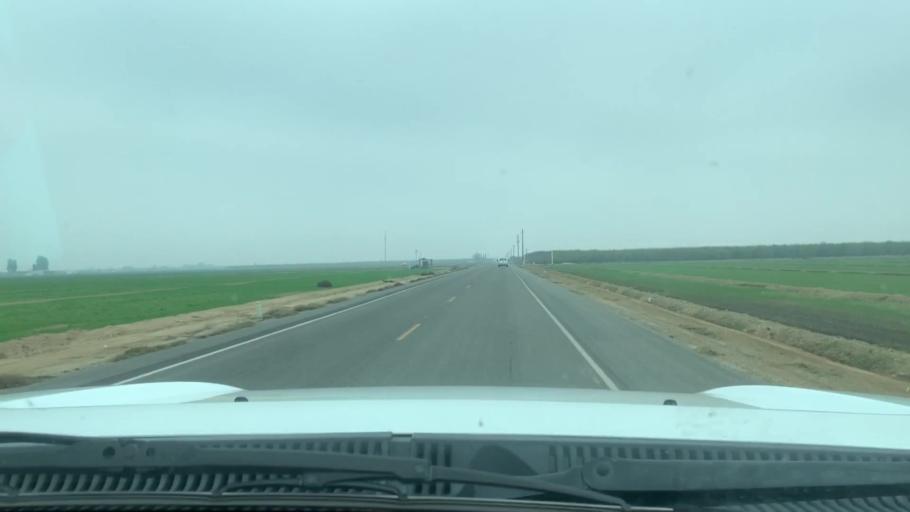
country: US
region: California
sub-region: Kern County
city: Wasco
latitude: 35.5002
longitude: -119.3795
